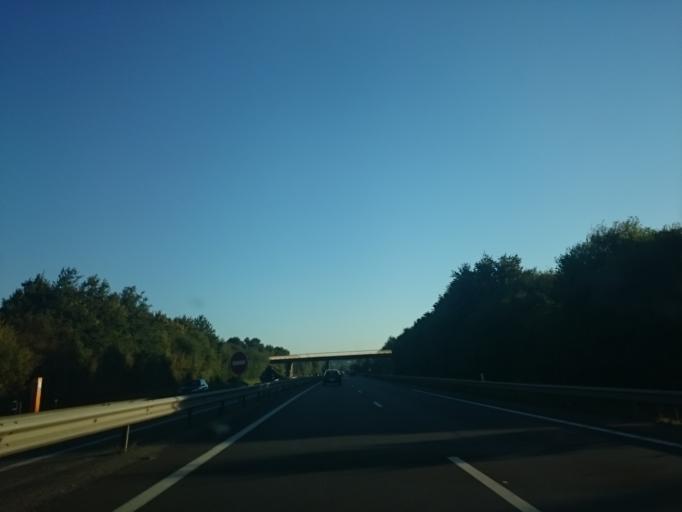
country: FR
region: Brittany
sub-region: Departement d'Ille-et-Vilaine
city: Orgeres
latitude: 48.0086
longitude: -1.6920
